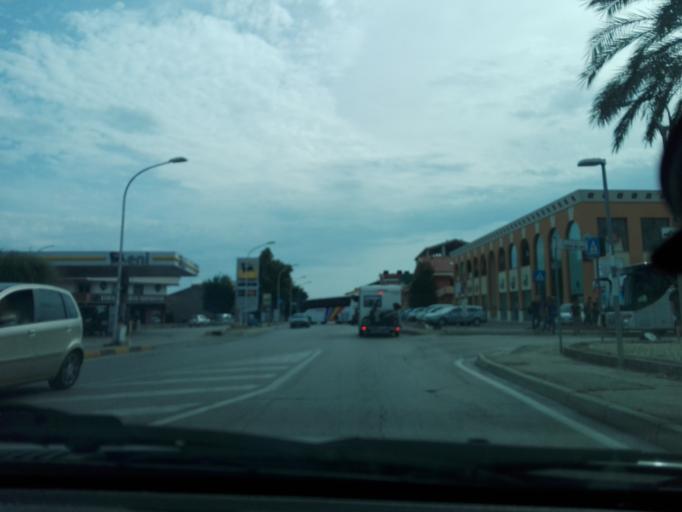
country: IT
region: Abruzzo
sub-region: Provincia di Pescara
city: San Martino Bassa
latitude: 42.5213
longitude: 14.1387
